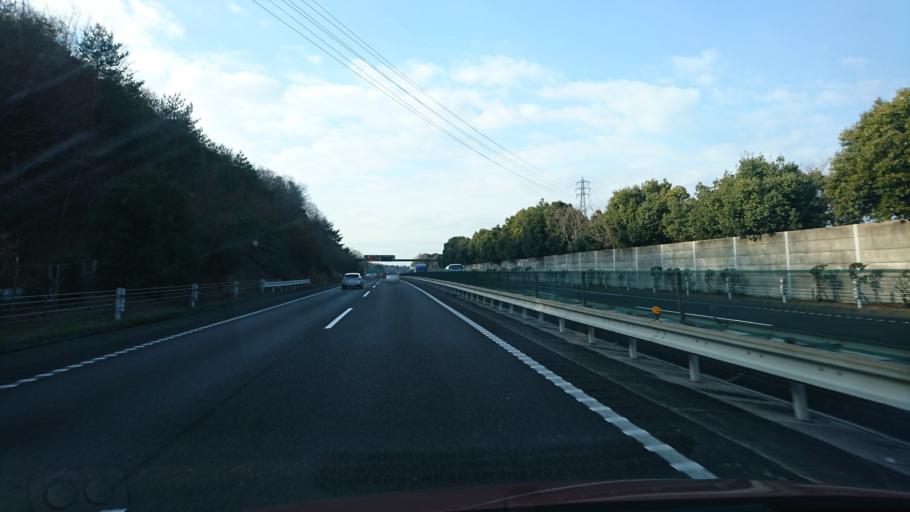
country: JP
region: Hyogo
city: Tatsunocho-tominaga
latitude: 34.8395
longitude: 134.5122
